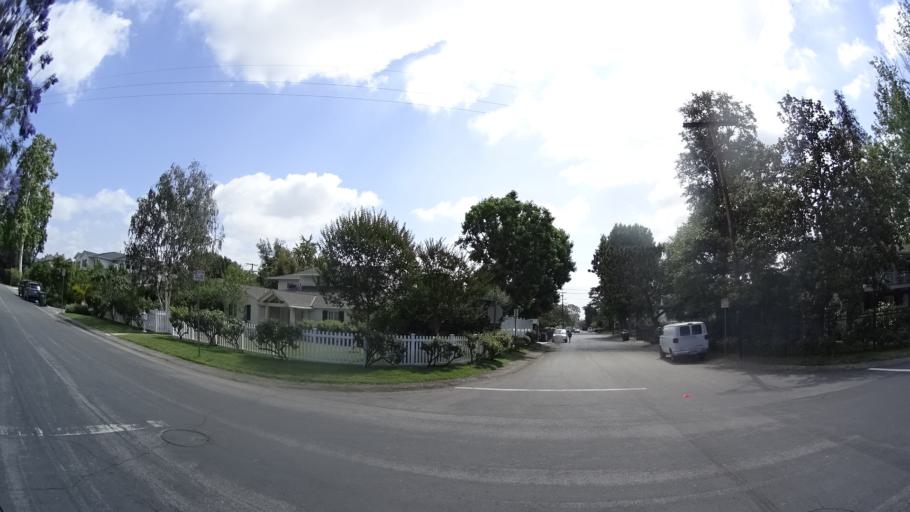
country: US
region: California
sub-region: Los Angeles County
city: Universal City
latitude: 34.1540
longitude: -118.3572
